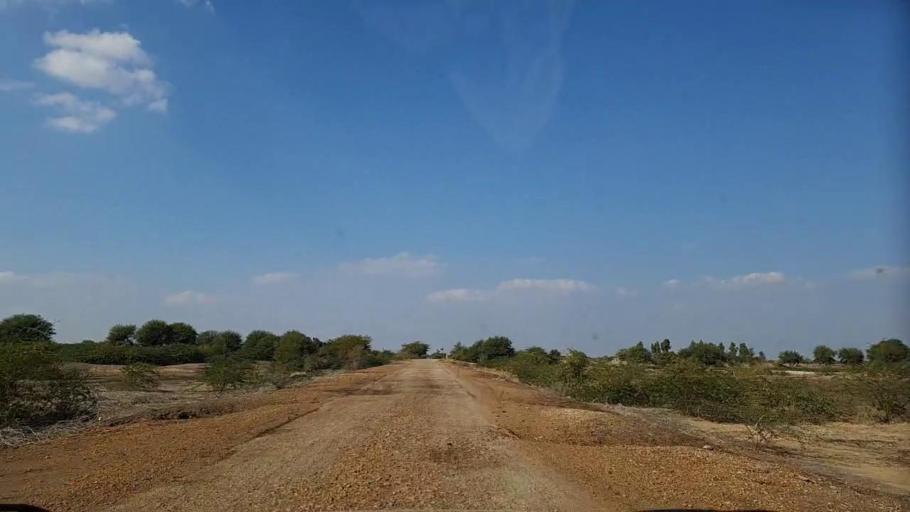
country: PK
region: Sindh
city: Pithoro
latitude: 25.6159
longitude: 69.3565
